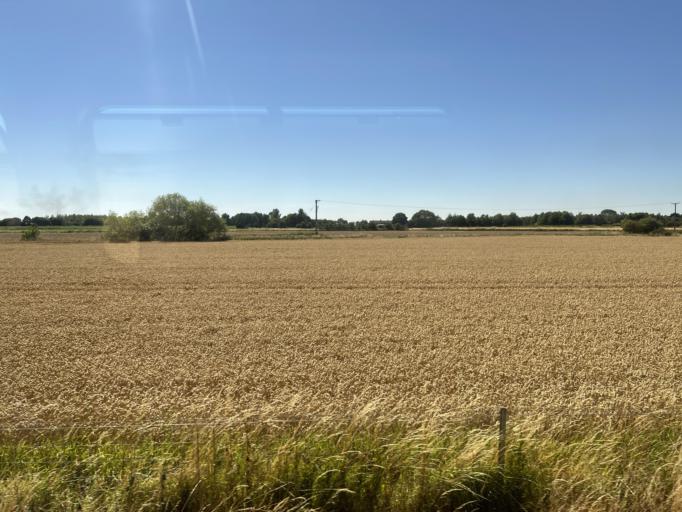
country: GB
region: England
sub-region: Lincolnshire
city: Wainfleet All Saints
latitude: 53.1123
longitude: 0.2191
